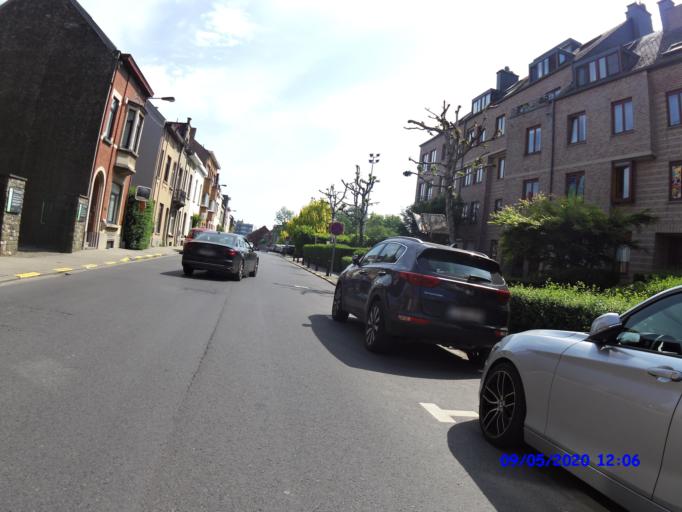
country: BE
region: Flanders
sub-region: Provincie Vlaams-Brabant
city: Kraainem
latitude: 50.8421
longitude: 4.4526
